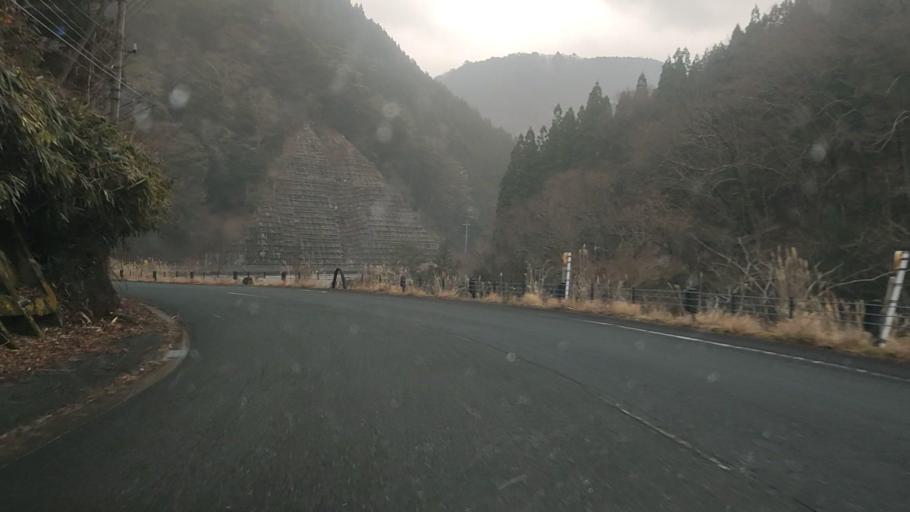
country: JP
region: Kumamoto
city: Matsubase
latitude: 32.5488
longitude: 130.9370
